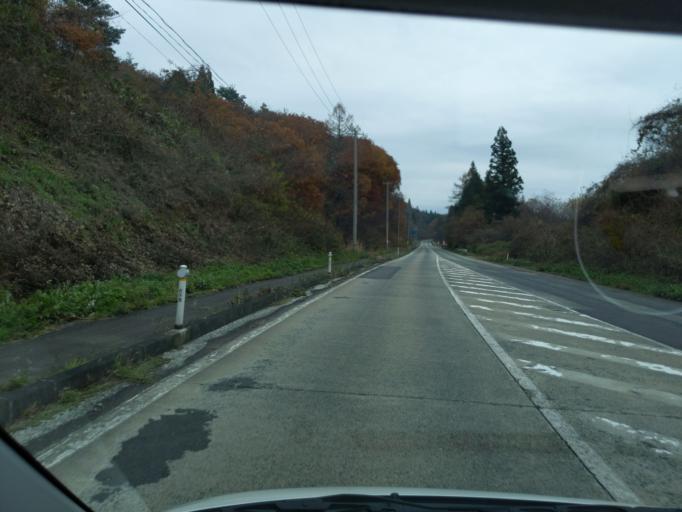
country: JP
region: Iwate
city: Kitakami
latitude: 39.3007
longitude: 141.2037
